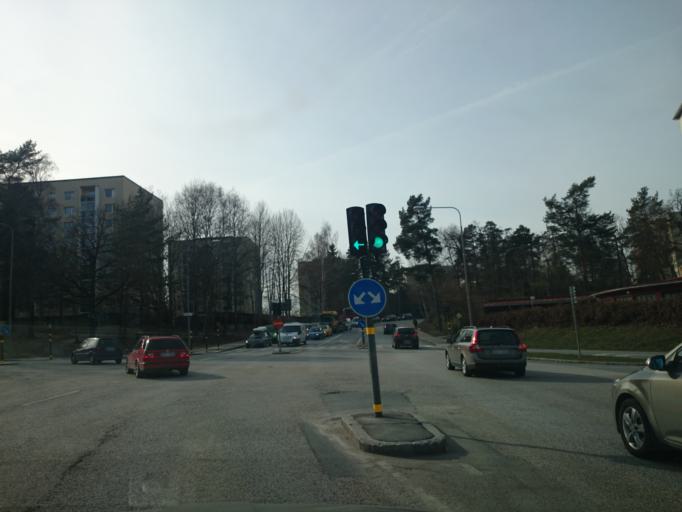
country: SE
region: Stockholm
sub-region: Stockholms Kommun
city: Arsta
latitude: 59.2357
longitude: 18.0965
